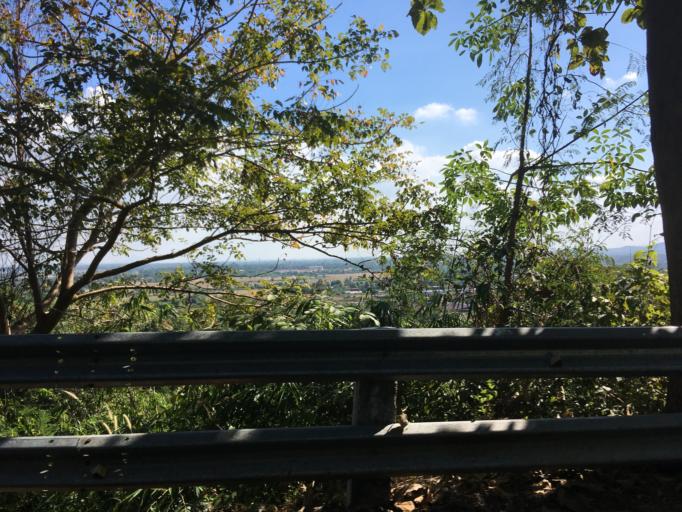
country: MM
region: Mon
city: Mawlamyine
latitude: 16.4744
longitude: 97.6303
